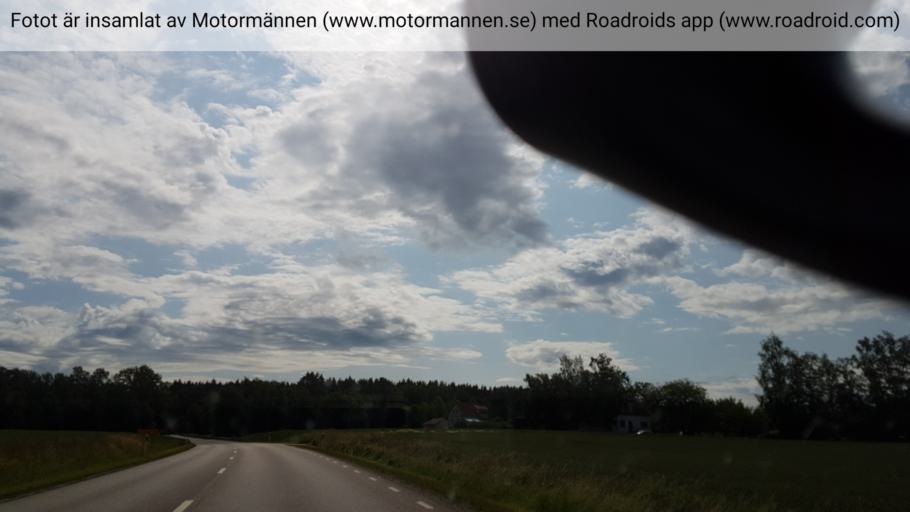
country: SE
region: Vaestra Goetaland
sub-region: Grastorps Kommun
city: Graestorp
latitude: 58.3290
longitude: 12.6964
